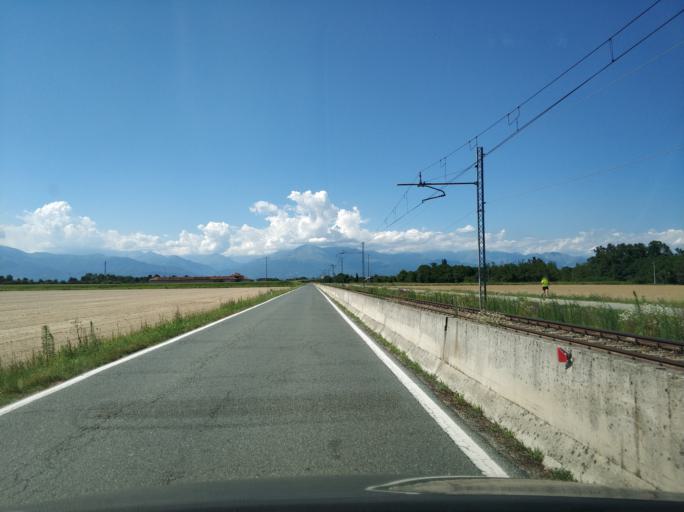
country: IT
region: Piedmont
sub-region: Provincia di Torino
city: Bosconero
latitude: 45.2454
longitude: 7.7711
